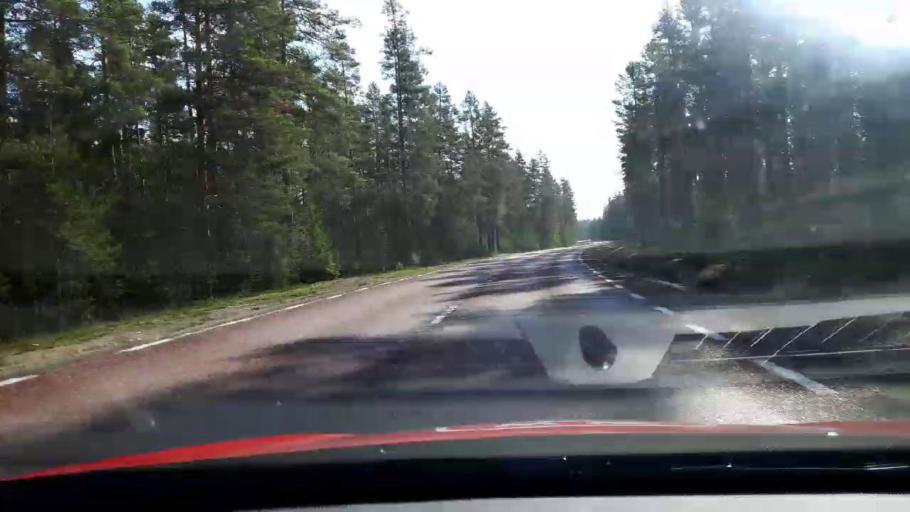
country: SE
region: Gaevleborg
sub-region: Ljusdals Kommun
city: Farila
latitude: 61.9195
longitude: 15.6128
